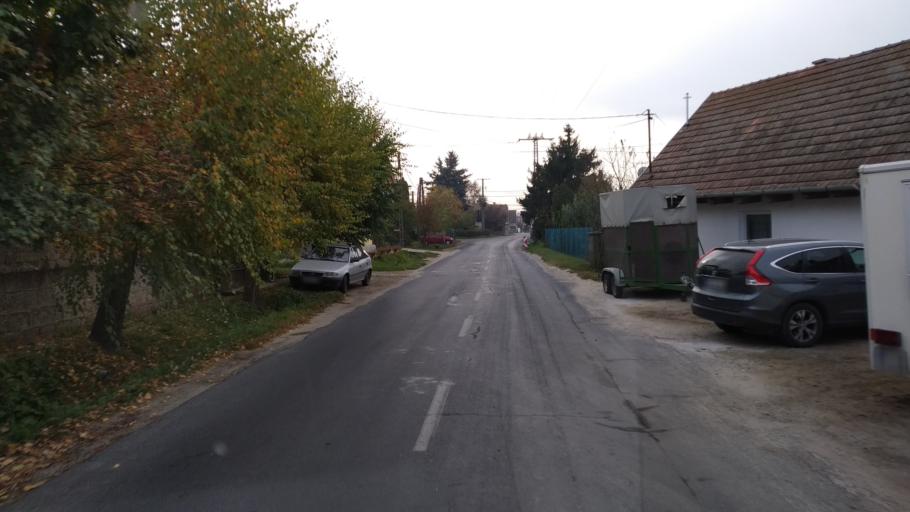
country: HU
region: Pest
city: Tahitotfalu
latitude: 47.7575
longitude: 19.0866
